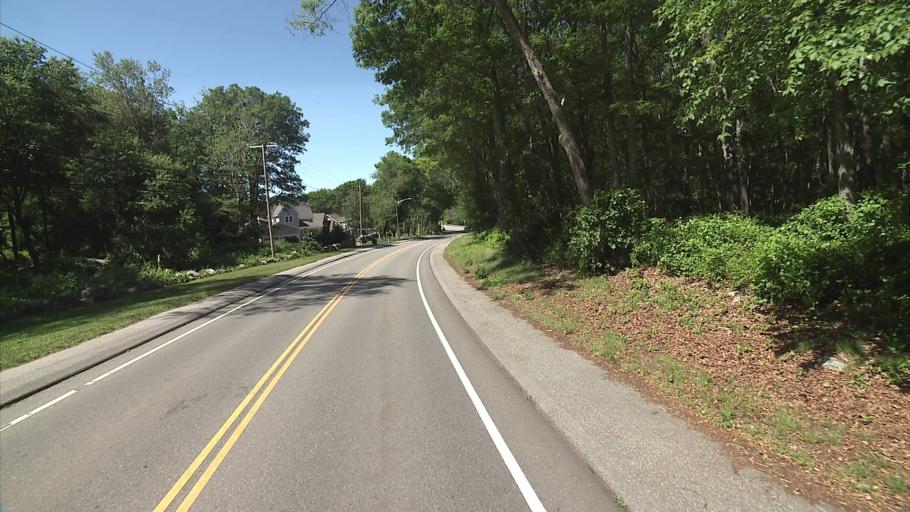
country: US
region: Connecticut
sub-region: New London County
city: Noank
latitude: 41.3391
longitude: -71.9889
